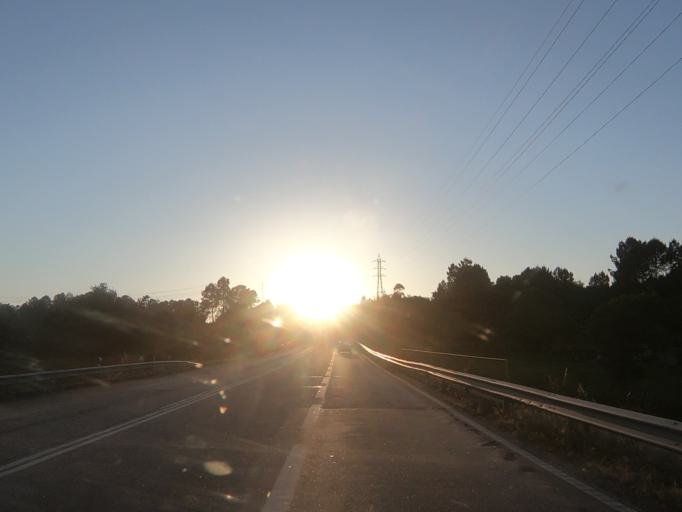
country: PT
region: Viseu
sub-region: Viseu
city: Rio de Loba
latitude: 40.6821
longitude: -7.8855
